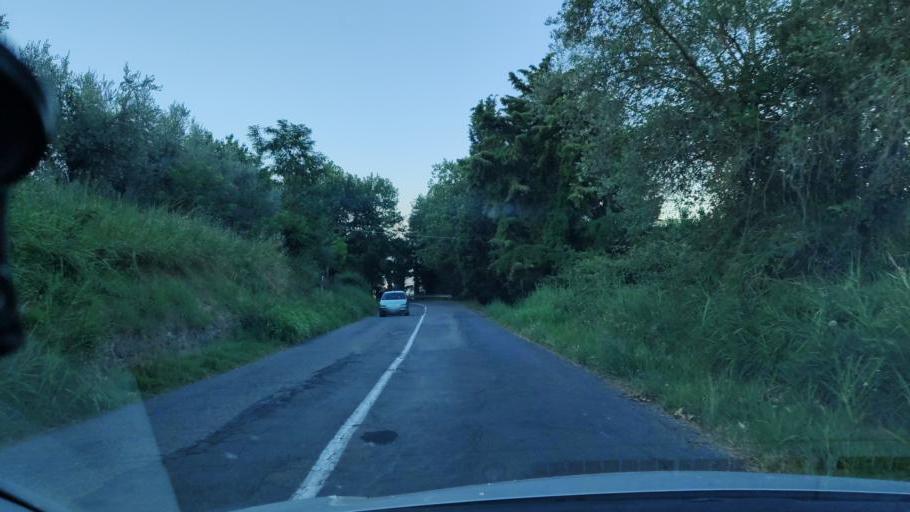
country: IT
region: Umbria
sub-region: Provincia di Terni
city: Giove
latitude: 42.5047
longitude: 12.3207
